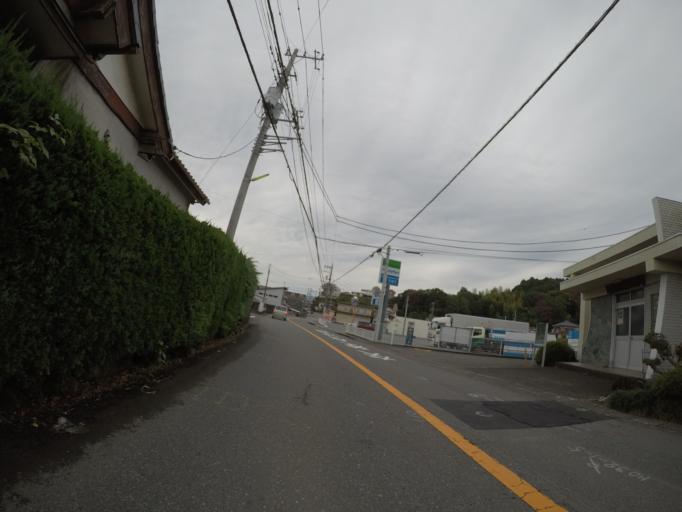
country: JP
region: Shizuoka
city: Fuji
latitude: 35.1907
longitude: 138.6866
